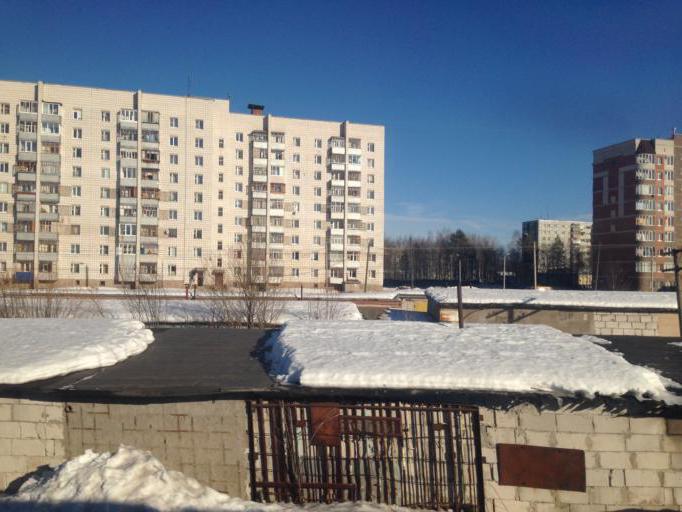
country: RU
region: Komi Republic
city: Ezhva
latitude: 61.7890
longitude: 50.7390
